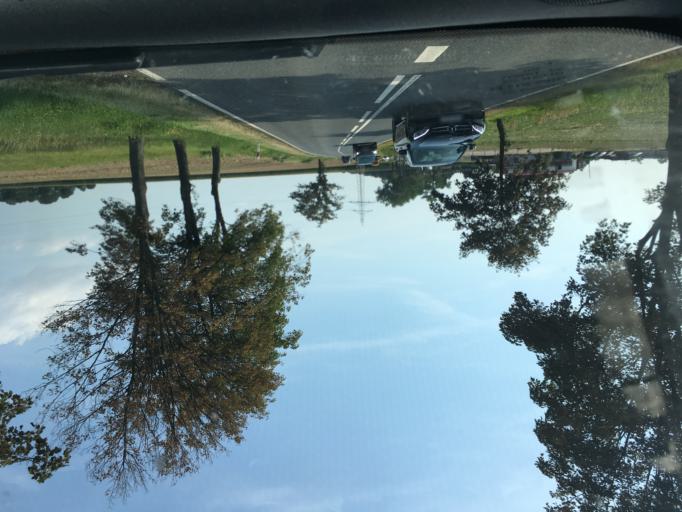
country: PL
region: Opole Voivodeship
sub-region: Powiat prudnicki
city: Laka Prudnicka
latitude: 50.4107
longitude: 17.5026
